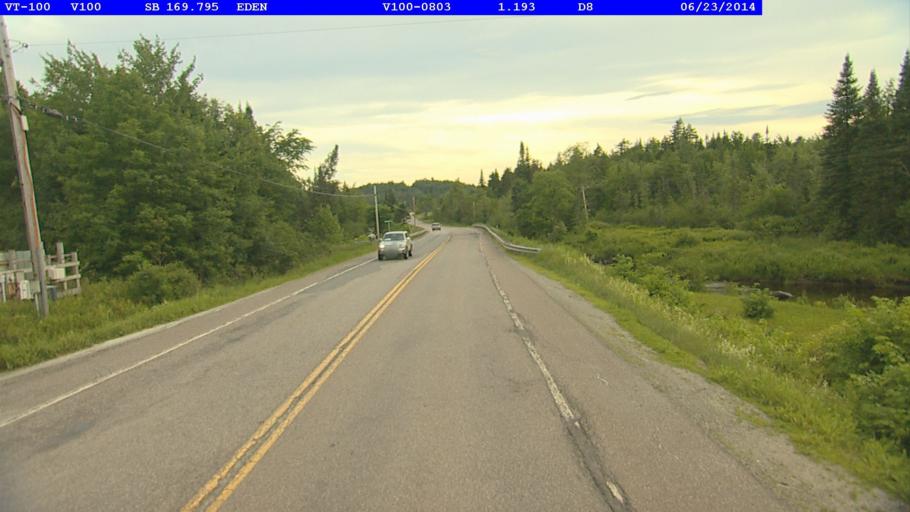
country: US
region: Vermont
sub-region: Lamoille County
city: Hyde Park
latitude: 44.6971
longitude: -72.5767
